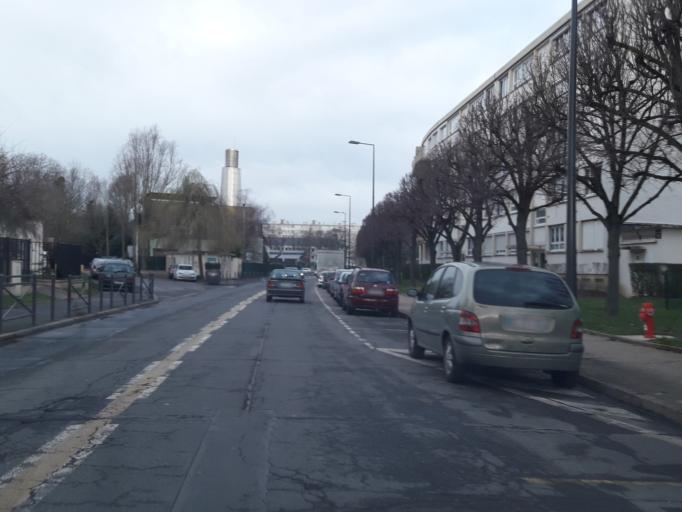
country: FR
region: Ile-de-France
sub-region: Departement de l'Essonne
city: Sainte-Genevieve-des-Bois
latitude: 48.6314
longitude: 2.3281
